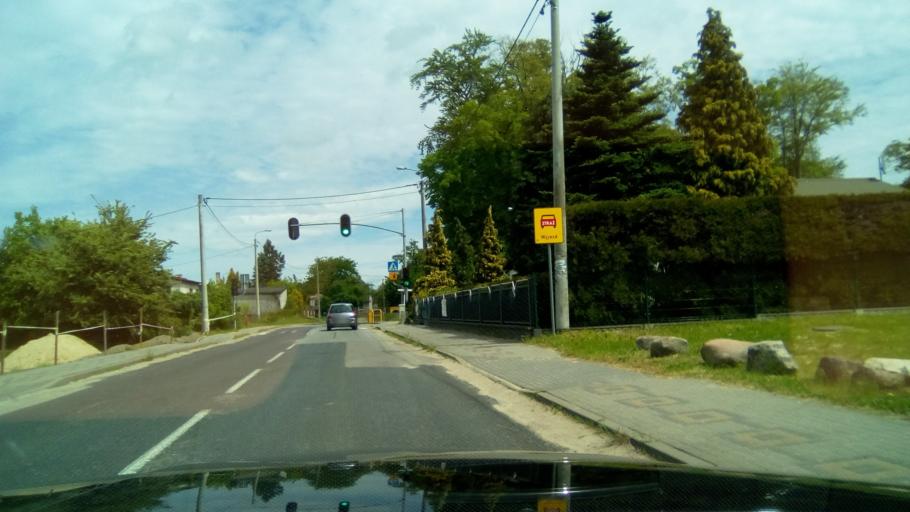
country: PL
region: Pomeranian Voivodeship
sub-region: Powiat leborski
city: Cewice
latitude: 54.4380
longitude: 17.7383
